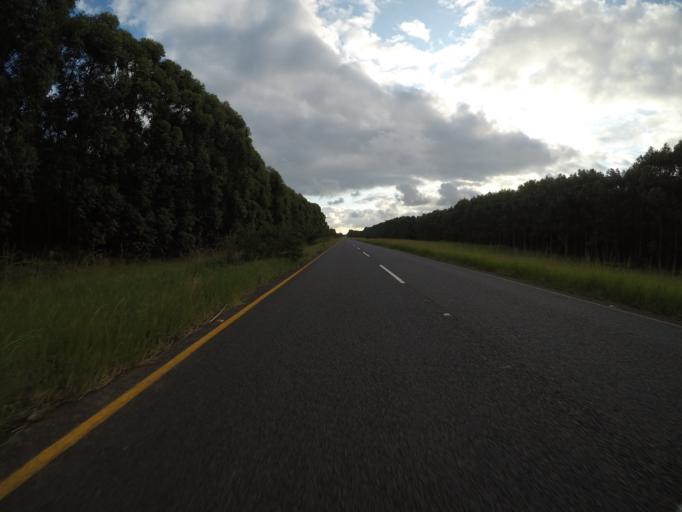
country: ZA
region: KwaZulu-Natal
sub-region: uMkhanyakude District Municipality
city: Mtubatuba
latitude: -28.3924
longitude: 32.2243
